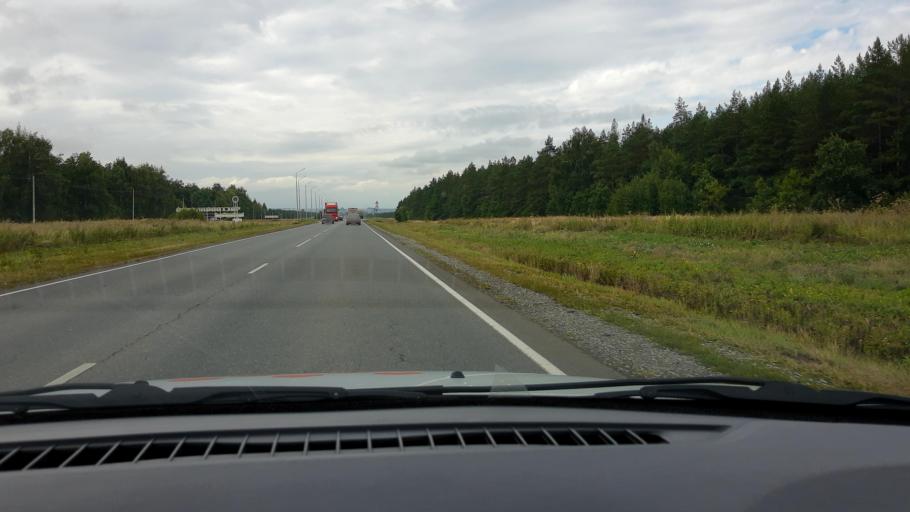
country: RU
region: Tatarstan
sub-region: Alekseyevskiy Rayon
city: Alekseyevskoye
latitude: 55.3102
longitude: 50.3474
